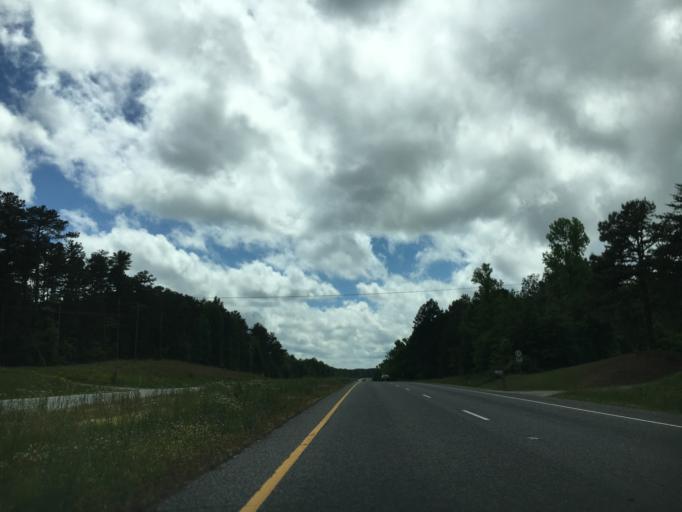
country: US
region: Virginia
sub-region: Mecklenburg County
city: Clarksville
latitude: 36.6468
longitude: -78.5028
